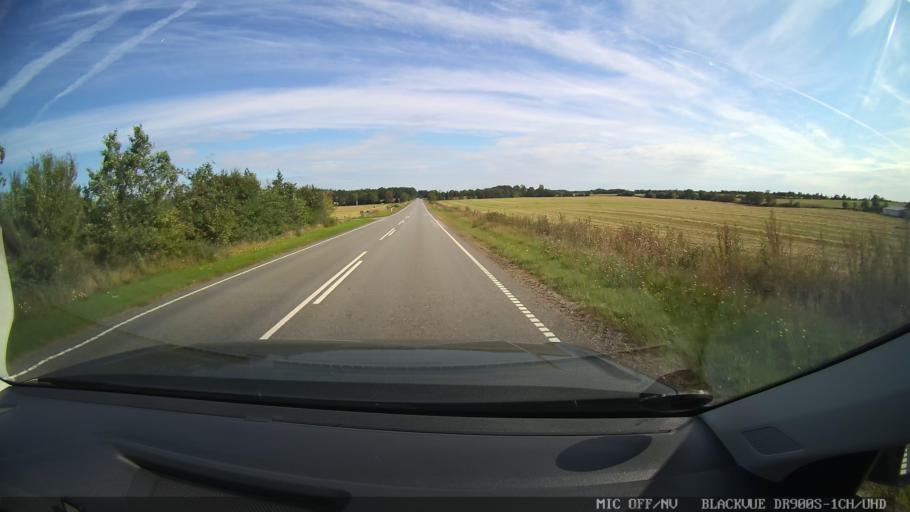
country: DK
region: North Denmark
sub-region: Mariagerfjord Kommune
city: Hadsund
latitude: 56.7816
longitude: 10.0134
